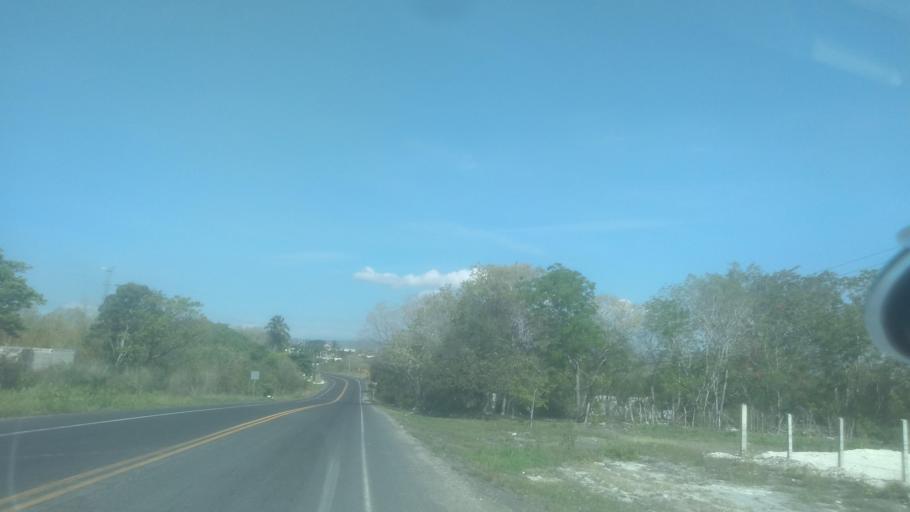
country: MX
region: Veracruz
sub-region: Emiliano Zapata
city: Plan del Rio
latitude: 19.3934
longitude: -96.6219
